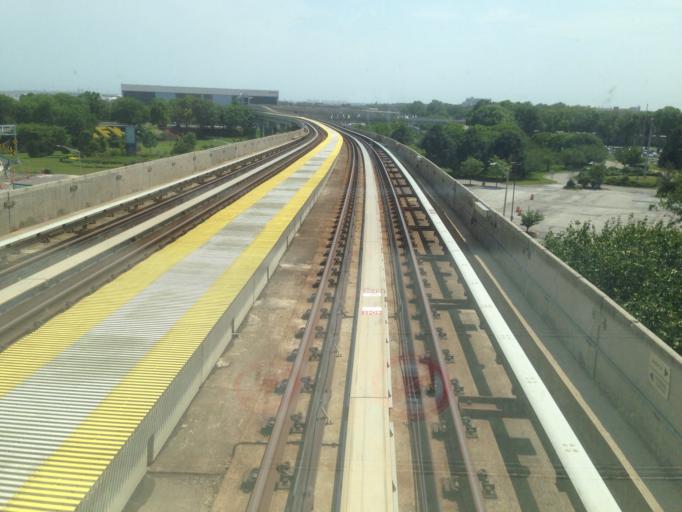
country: US
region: New York
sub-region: Queens County
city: Jamaica
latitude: 40.6652
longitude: -73.8030
